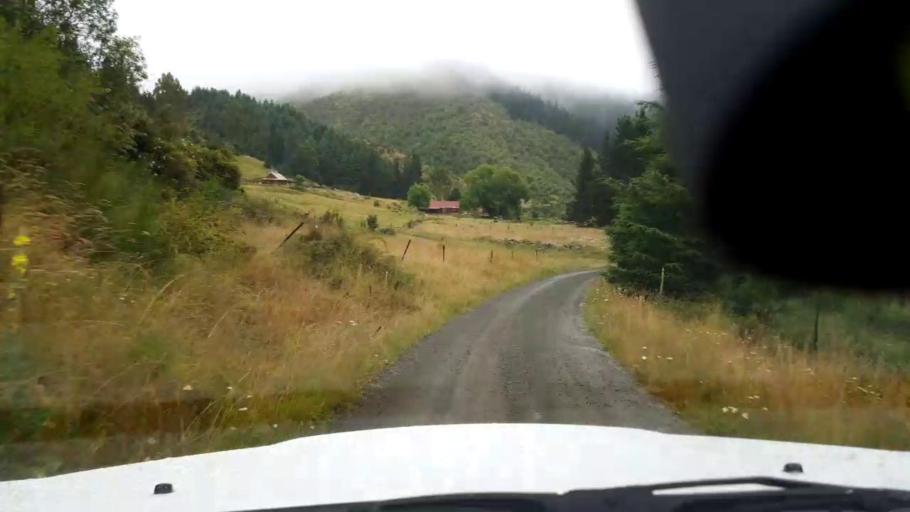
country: NZ
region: Canterbury
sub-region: Timaru District
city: Pleasant Point
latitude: -44.0470
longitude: 171.0239
